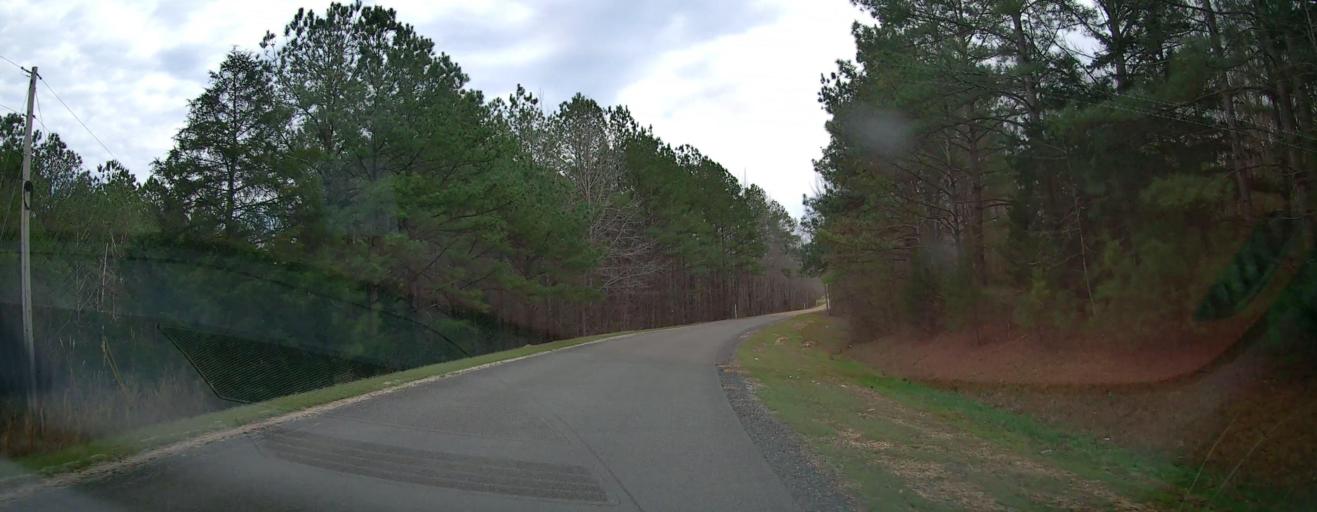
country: US
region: Mississippi
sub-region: Itawamba County
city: Fulton
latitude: 34.2134
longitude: -88.2009
